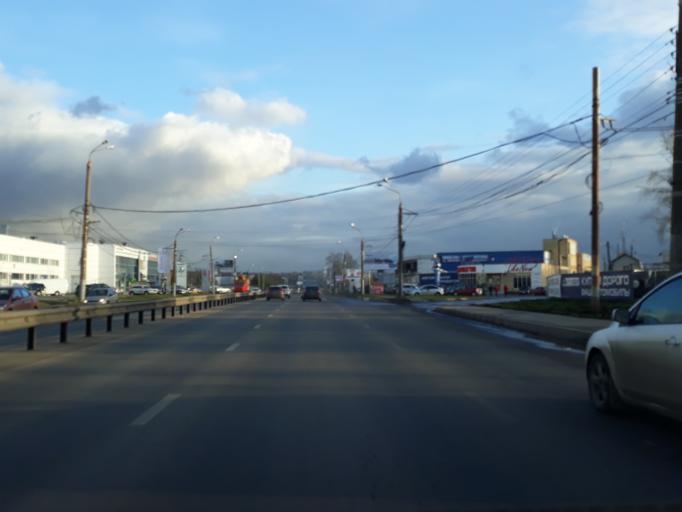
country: RU
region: Nizjnij Novgorod
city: Nizhniy Novgorod
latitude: 56.3018
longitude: 43.9210
